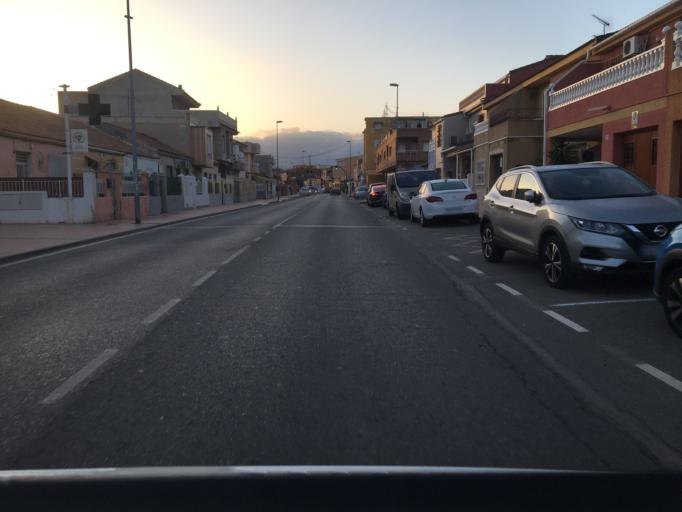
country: ES
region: Murcia
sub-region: Murcia
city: Cartagena
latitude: 37.6296
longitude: -0.9894
